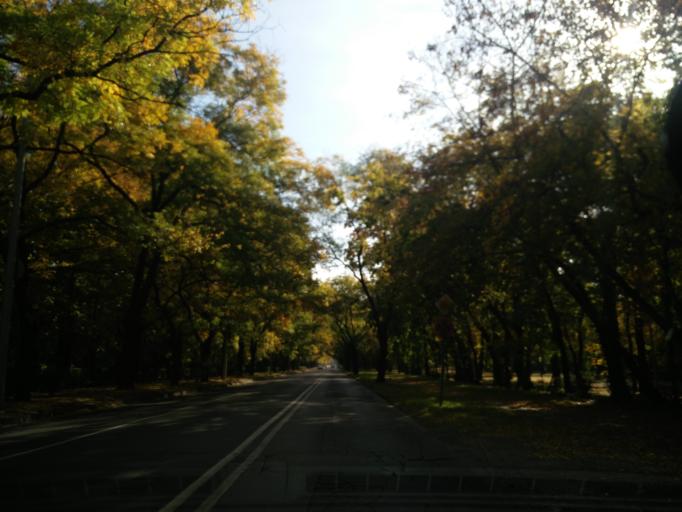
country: HU
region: Budapest
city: Budapest VIII. keruelet
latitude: 47.4815
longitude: 19.1055
